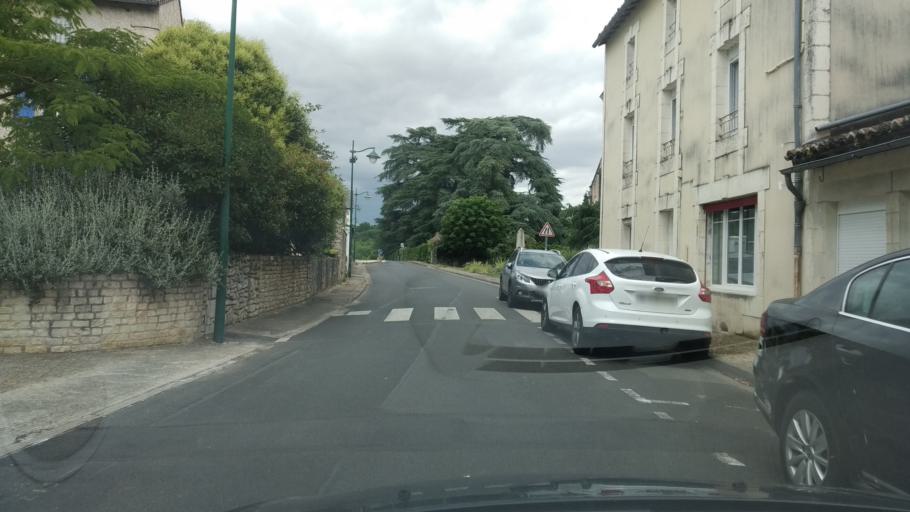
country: FR
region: Poitou-Charentes
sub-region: Departement de la Vienne
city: Vouneuil-sous-Biard
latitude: 46.5758
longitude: 0.2733
